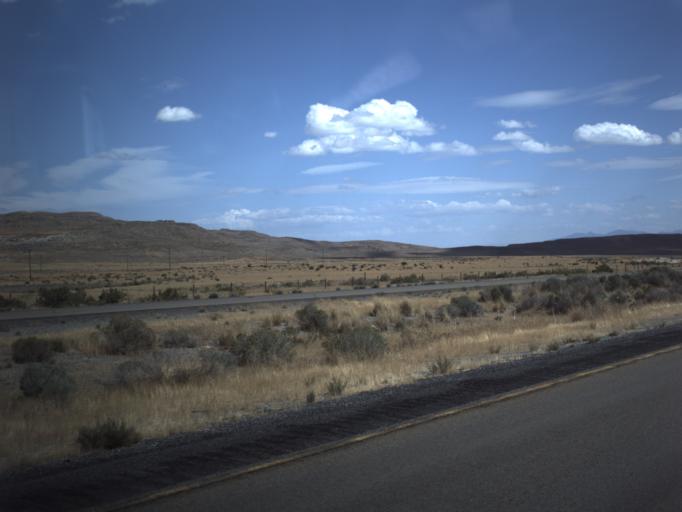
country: US
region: Utah
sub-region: Tooele County
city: Grantsville
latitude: 40.7976
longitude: -112.8453
